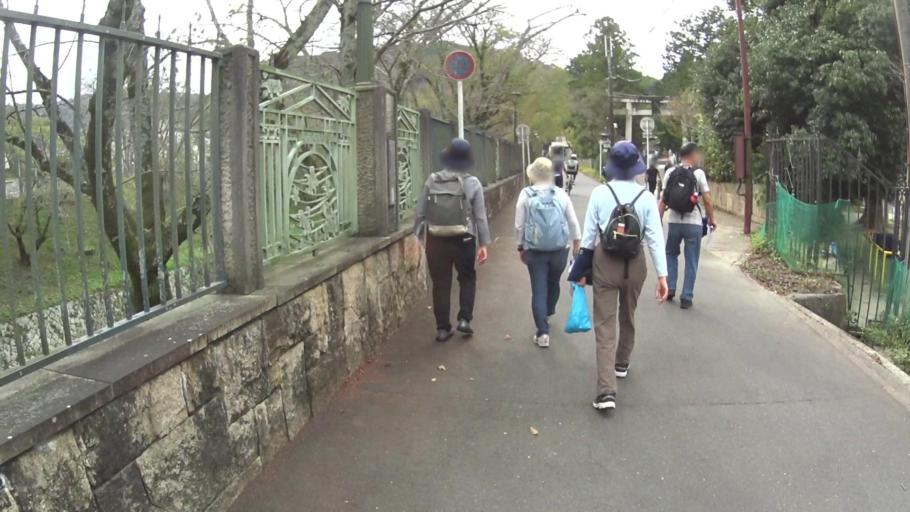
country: JP
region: Shiga Prefecture
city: Hikone
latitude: 35.2710
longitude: 136.3751
